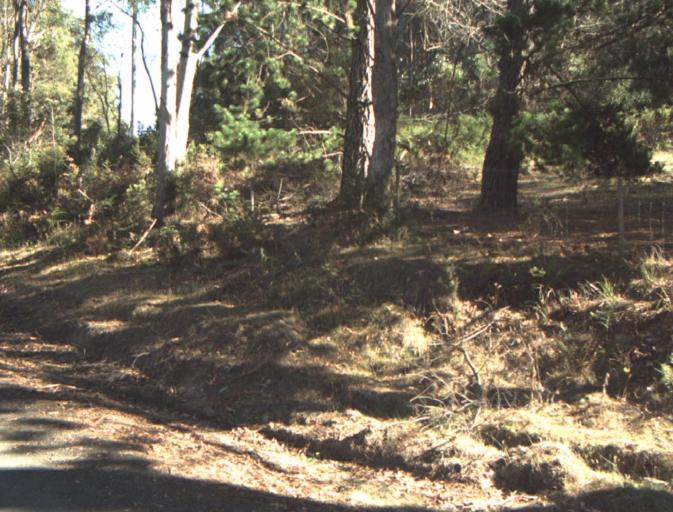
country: AU
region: Tasmania
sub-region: Launceston
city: Newstead
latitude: -41.3106
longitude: 147.3354
